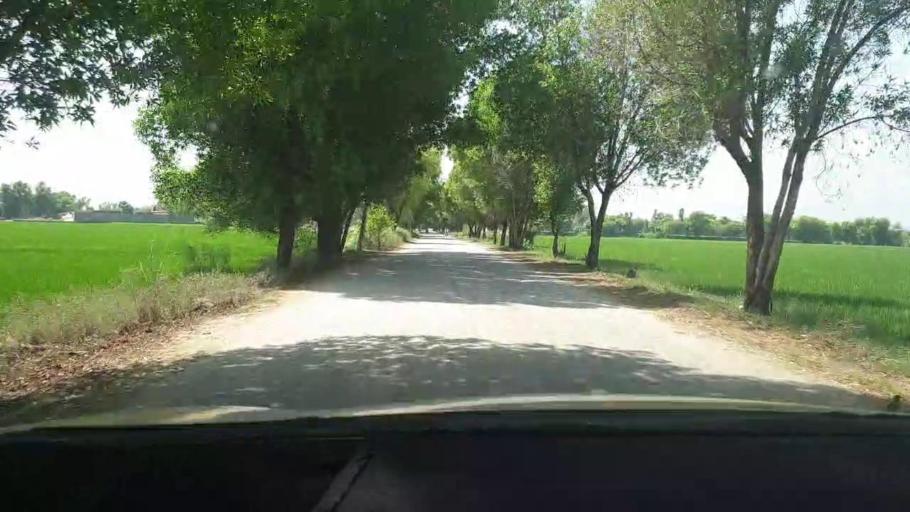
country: PK
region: Sindh
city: Miro Khan
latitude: 27.6718
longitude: 68.0528
